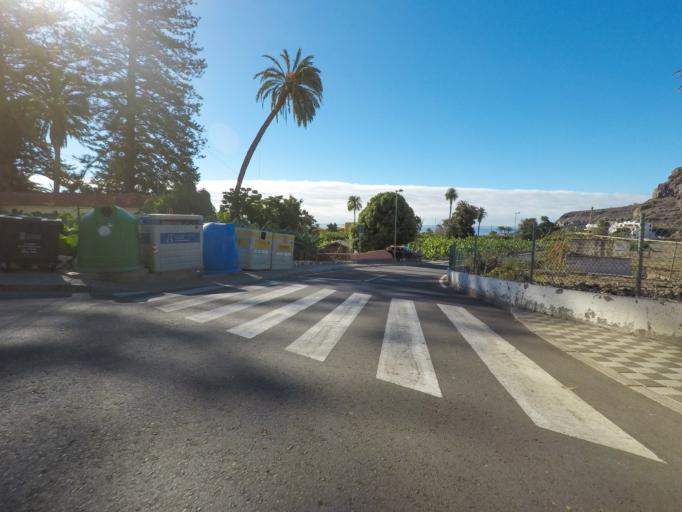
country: ES
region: Canary Islands
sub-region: Provincia de Santa Cruz de Tenerife
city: Alajero
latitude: 28.0321
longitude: -17.1931
